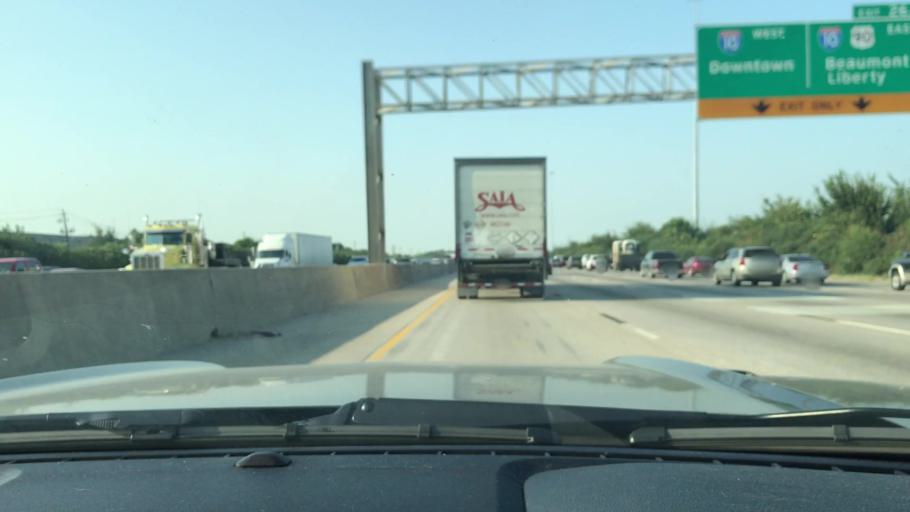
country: US
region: Texas
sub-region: Harris County
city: Jacinto City
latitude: 29.7560
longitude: -95.2651
